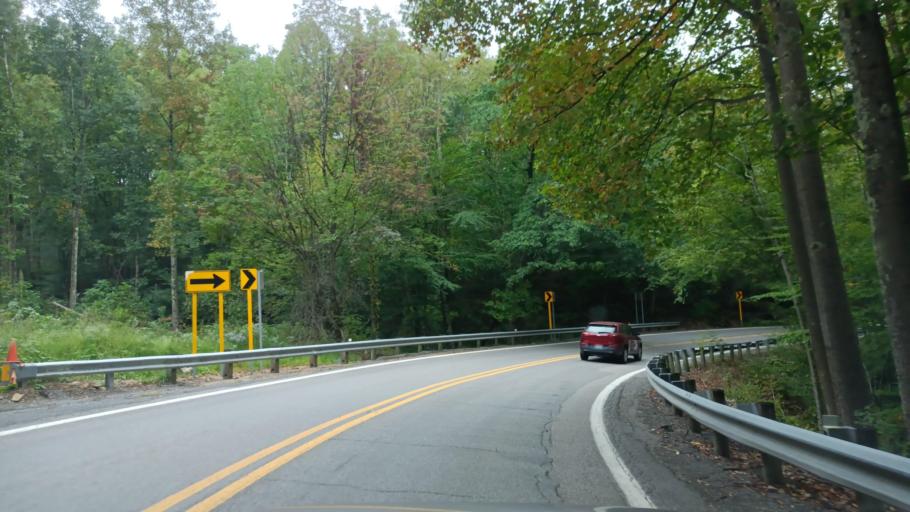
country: US
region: West Virginia
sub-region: Preston County
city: Kingwood
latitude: 39.3262
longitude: -79.7494
